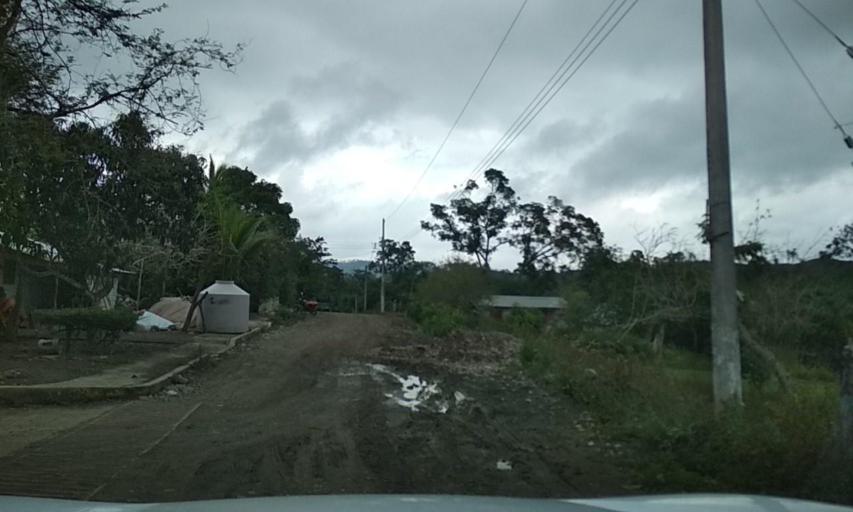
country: MX
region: Veracruz
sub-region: Coatzintla
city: Manuel Maria Contreras
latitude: 20.3501
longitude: -97.4689
